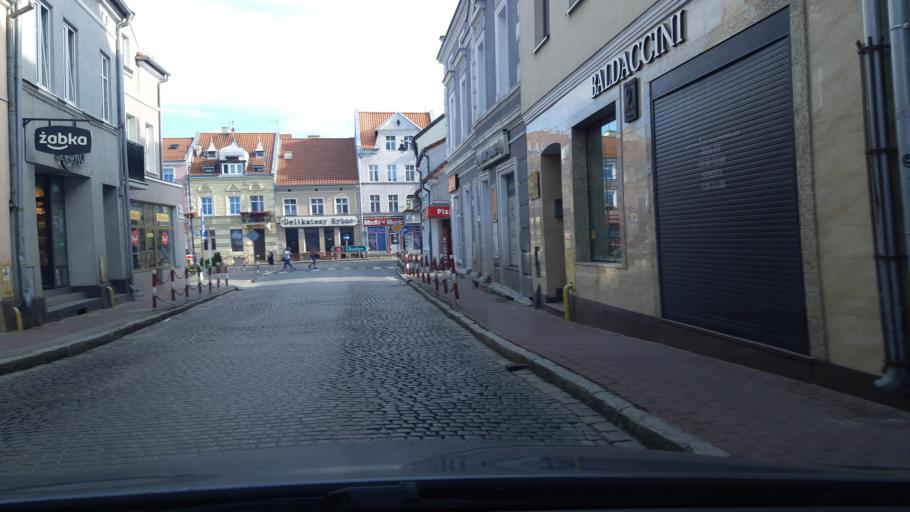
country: PL
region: Warmian-Masurian Voivodeship
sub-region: Powiat mragowski
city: Mragowo
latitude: 53.8720
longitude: 21.3038
